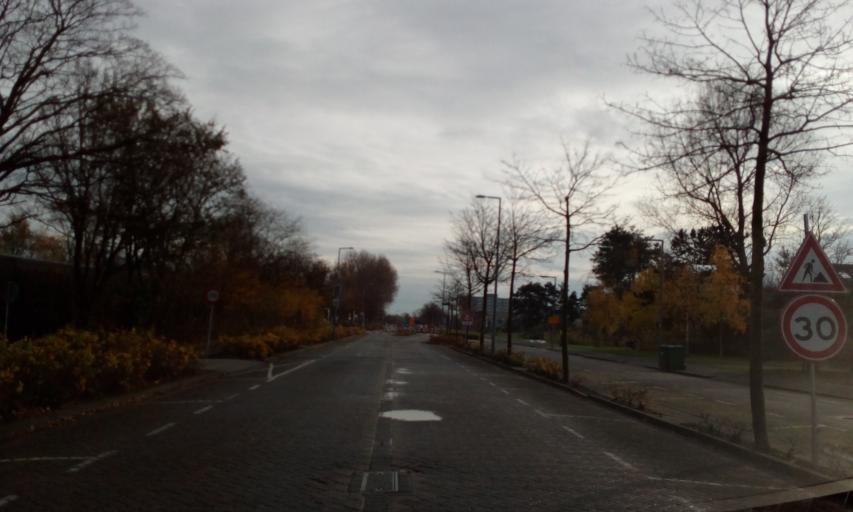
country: NL
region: South Holland
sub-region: Gemeente Rotterdam
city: Hoek van Holland
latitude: 51.9887
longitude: 4.1254
